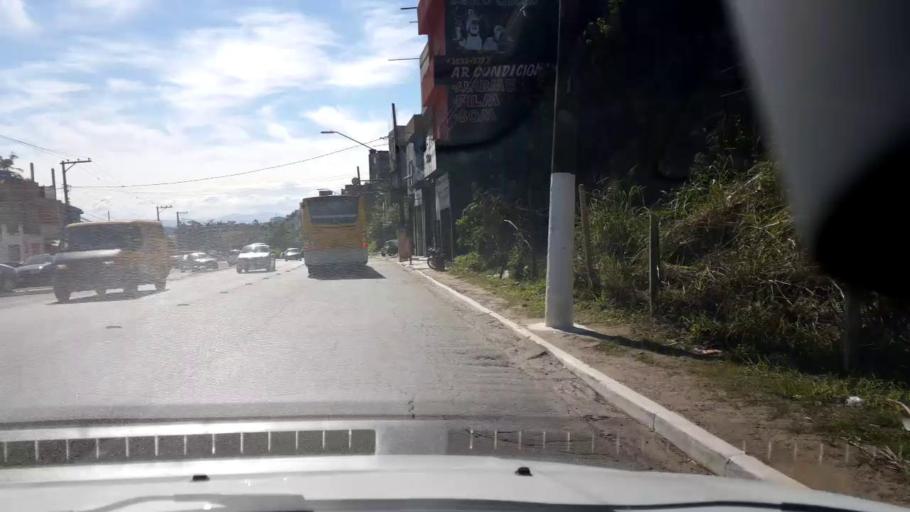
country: BR
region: Sao Paulo
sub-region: Ferraz De Vasconcelos
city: Ferraz de Vasconcelos
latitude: -23.5874
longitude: -46.4149
